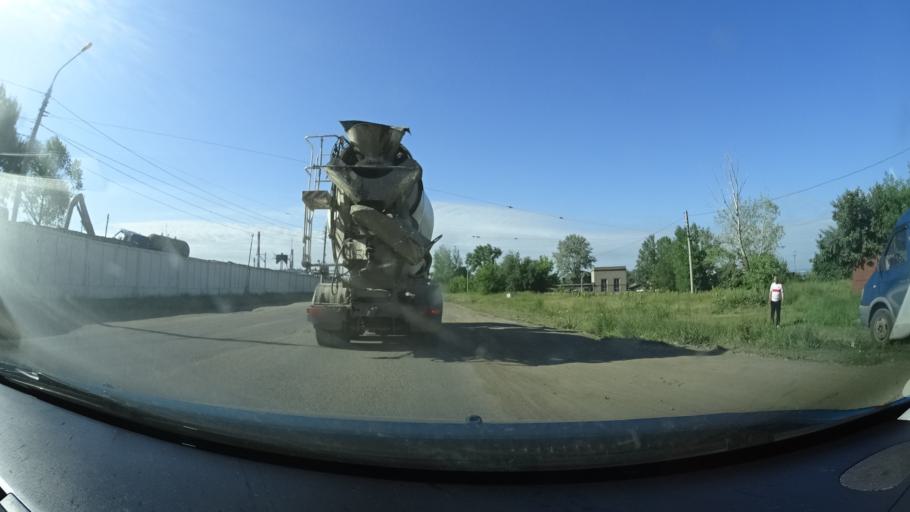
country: RU
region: Bashkortostan
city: Ufa
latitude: 54.8534
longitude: 56.0851
